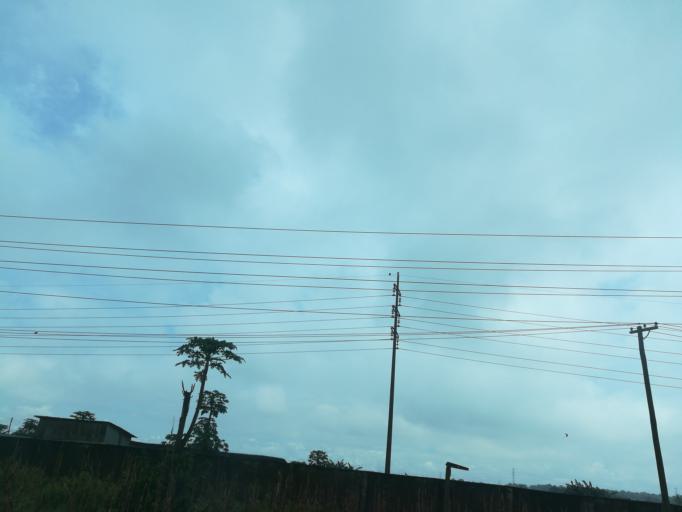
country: NG
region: Lagos
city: Ikorodu
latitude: 6.6536
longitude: 3.5193
